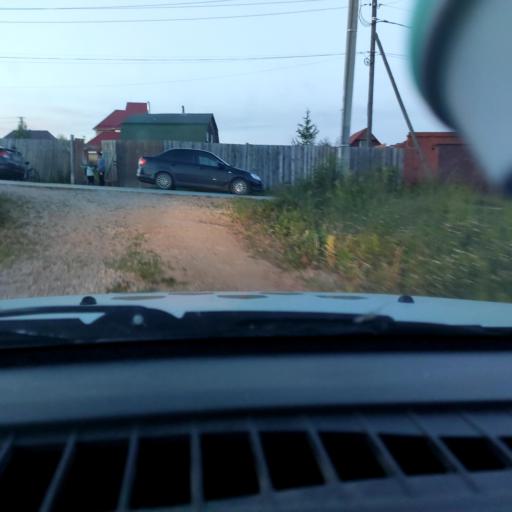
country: RU
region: Perm
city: Perm
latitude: 58.0374
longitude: 56.3916
